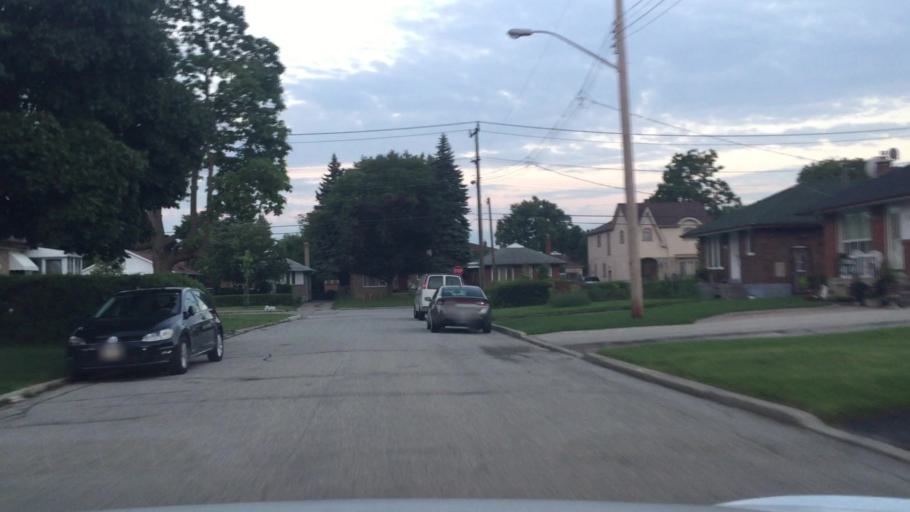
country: CA
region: Ontario
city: Scarborough
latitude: 43.7635
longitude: -79.3134
